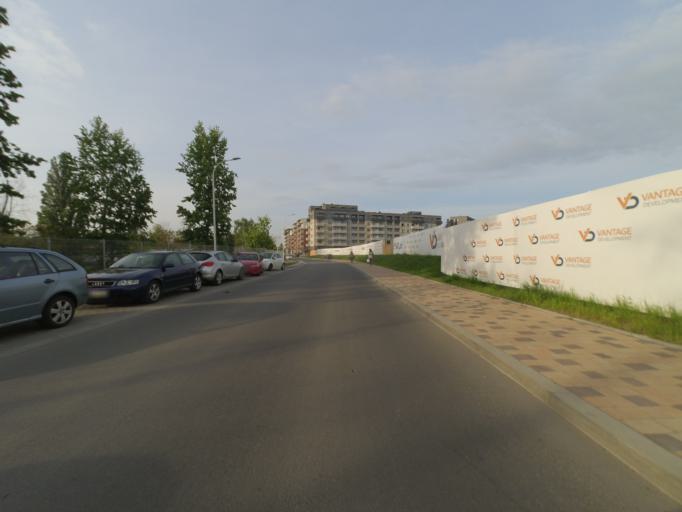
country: PL
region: Lower Silesian Voivodeship
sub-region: Powiat wroclawski
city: Wroclaw
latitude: 51.1271
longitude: 17.0392
